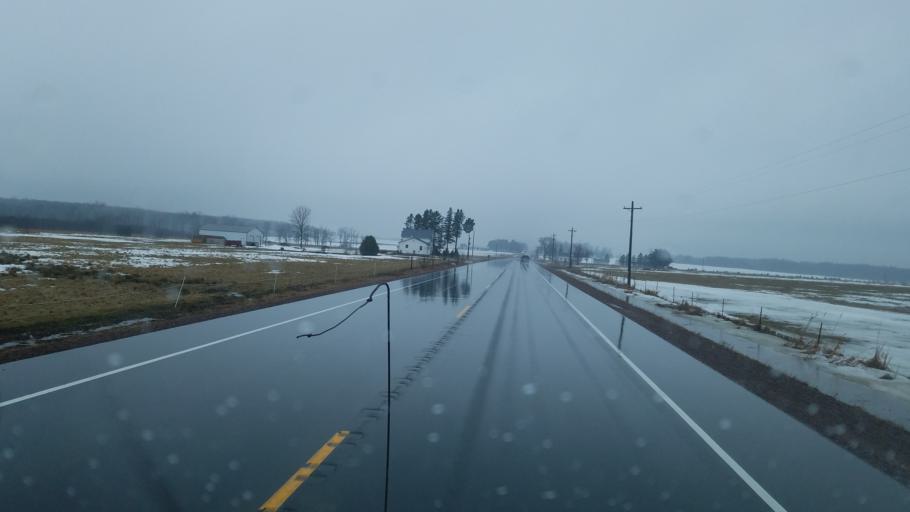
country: US
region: Wisconsin
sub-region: Marathon County
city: Spencer
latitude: 44.6561
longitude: -90.3109
